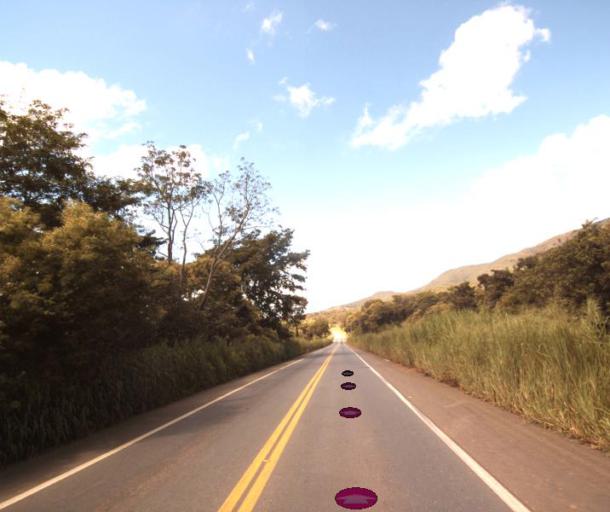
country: BR
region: Goias
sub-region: Jaragua
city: Jaragua
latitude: -15.7972
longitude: -49.3007
